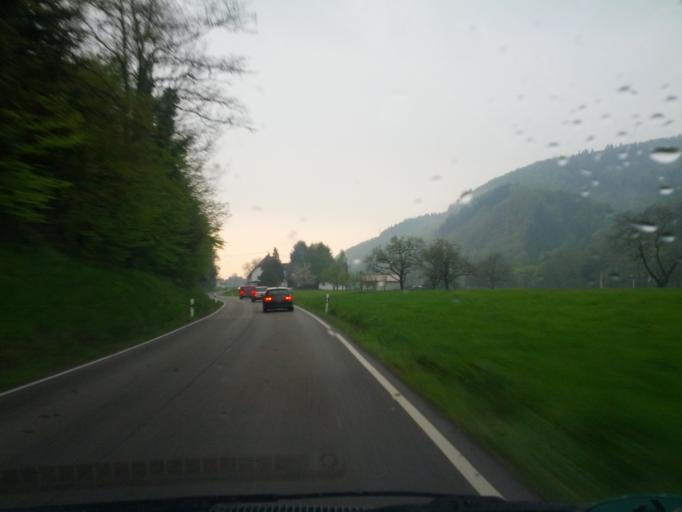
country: DE
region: Baden-Wuerttemberg
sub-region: Freiburg Region
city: Muenstertal/Schwarzwald
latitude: 47.8626
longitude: 7.7538
